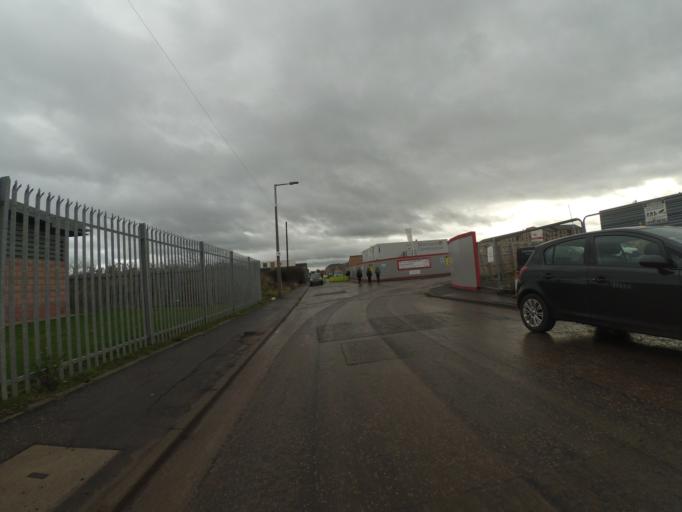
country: GB
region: Scotland
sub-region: West Lothian
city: Seafield
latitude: 55.9352
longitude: -3.1363
